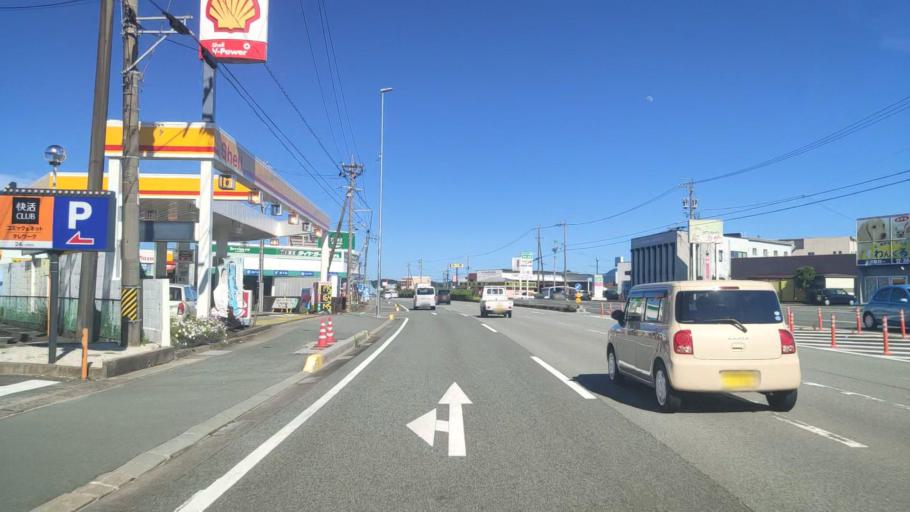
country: JP
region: Mie
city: Ise
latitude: 34.5060
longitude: 136.7286
